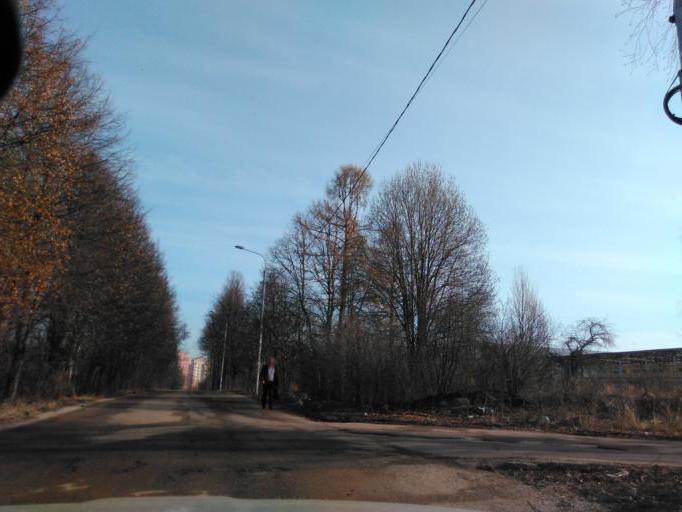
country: RU
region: Moscow
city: Zelenograd
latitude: 55.9654
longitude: 37.1612
